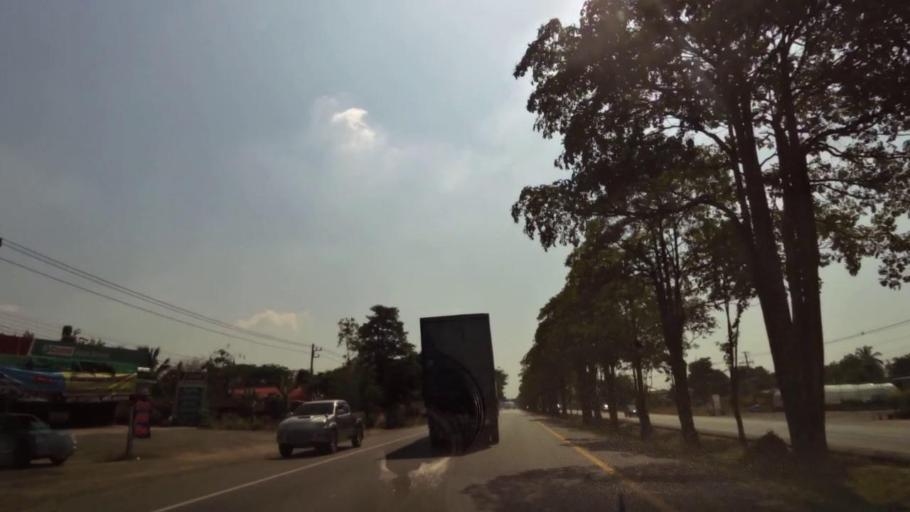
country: TH
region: Phichit
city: Bueng Na Rang
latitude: 16.1329
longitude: 100.1255
